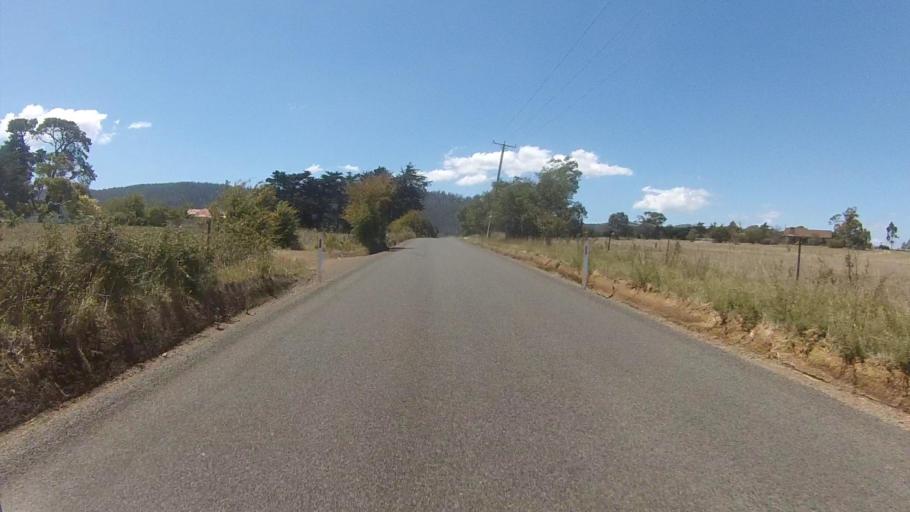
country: AU
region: Tasmania
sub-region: Sorell
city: Sorell
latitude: -42.7614
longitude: 147.6197
